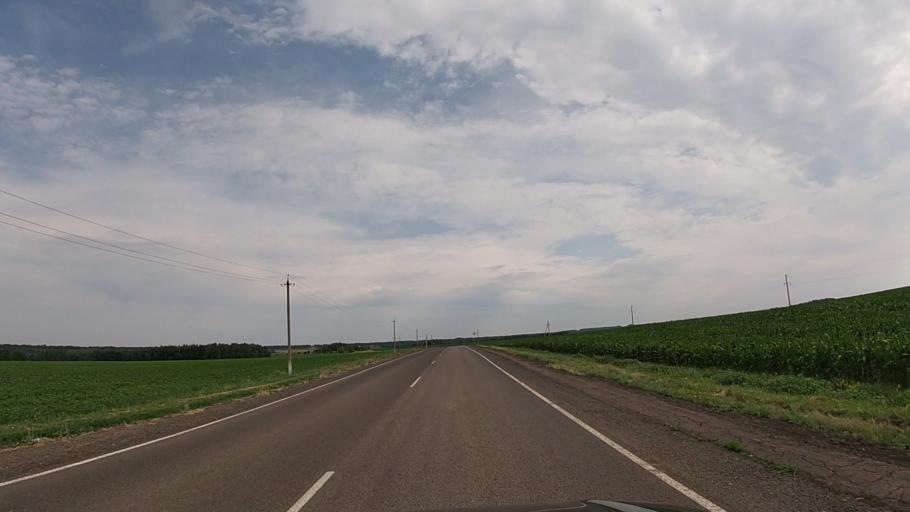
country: RU
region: Belgorod
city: Krasnaya Yaruga
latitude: 50.8182
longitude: 35.5021
